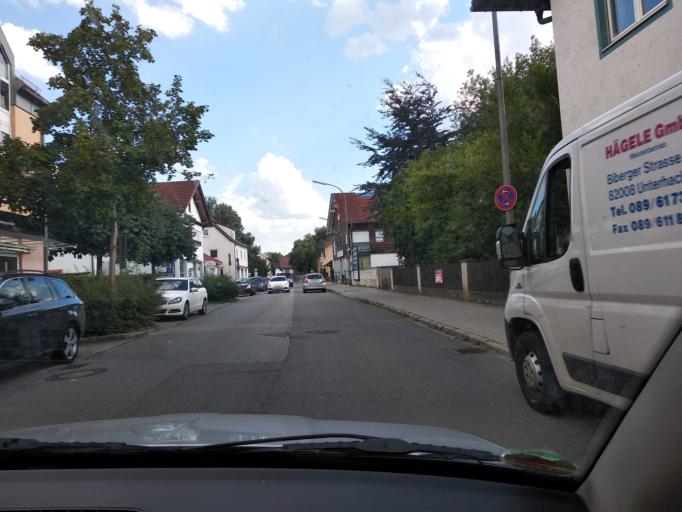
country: DE
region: Bavaria
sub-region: Upper Bavaria
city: Unterhaching
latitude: 48.0595
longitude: 11.6186
